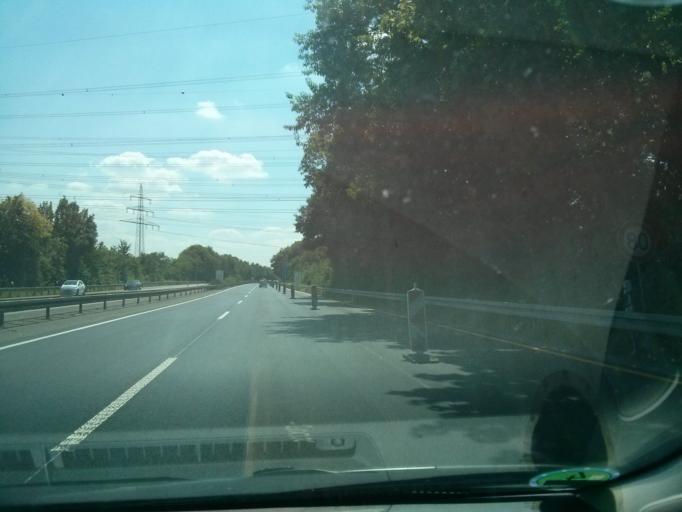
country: DE
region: North Rhine-Westphalia
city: Meckenheim
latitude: 50.6095
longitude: 7.0414
